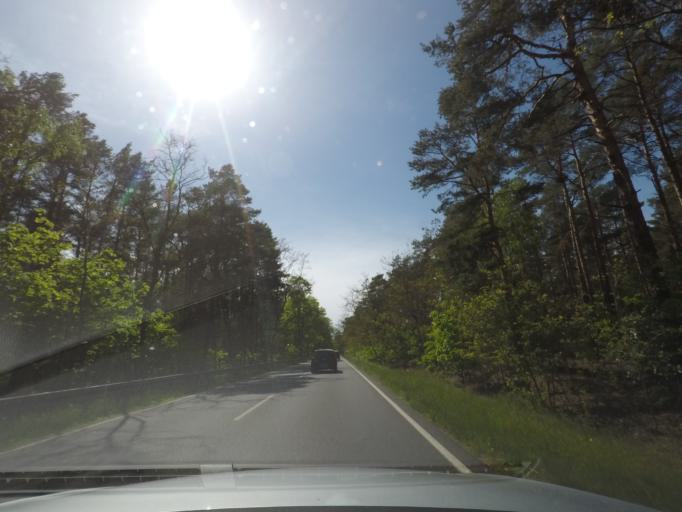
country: DE
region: Brandenburg
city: Luebben
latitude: 51.9460
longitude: 13.8364
